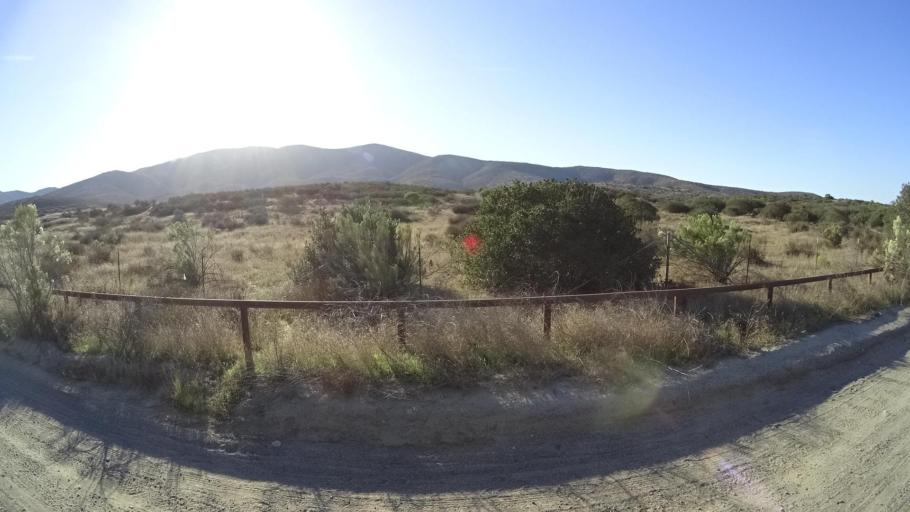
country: US
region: California
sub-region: San Diego County
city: Jamul
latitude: 32.6684
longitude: -116.9256
